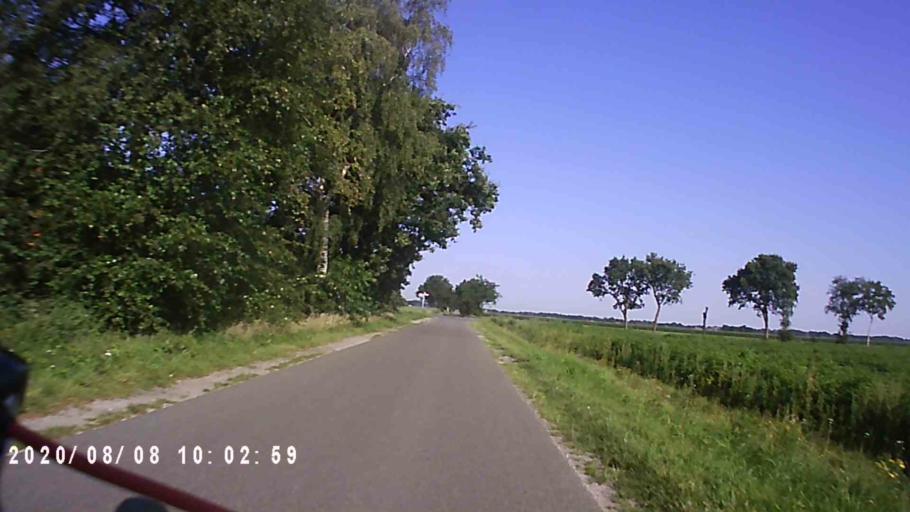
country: NL
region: Groningen
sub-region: Gemeente Leek
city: Leek
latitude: 53.1075
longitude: 6.3830
